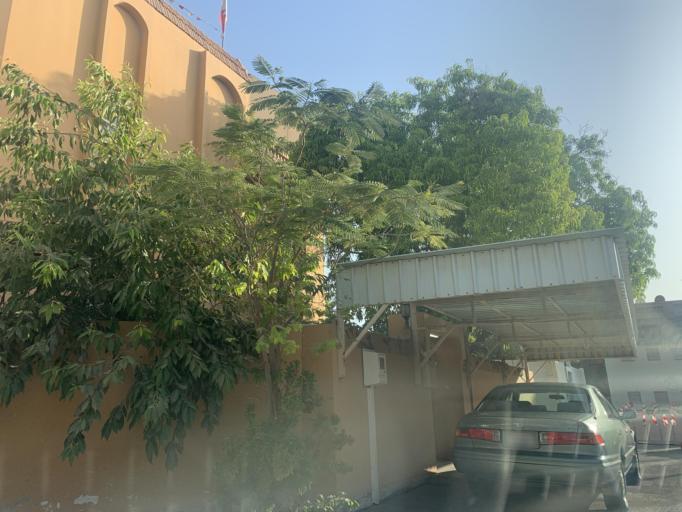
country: BH
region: Manama
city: Jidd Hafs
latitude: 26.2099
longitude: 50.4524
